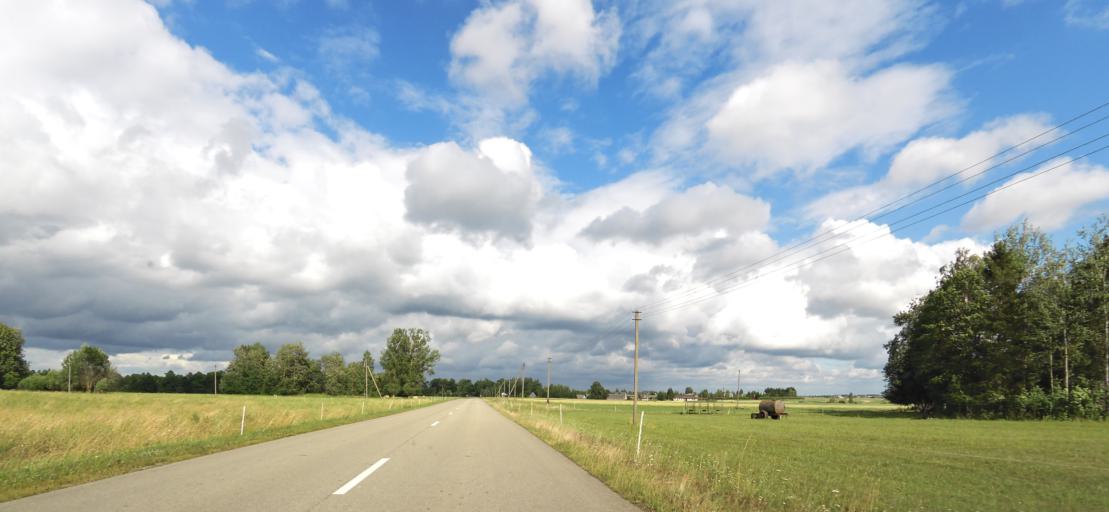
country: LT
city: Obeliai
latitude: 55.8998
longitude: 25.1546
